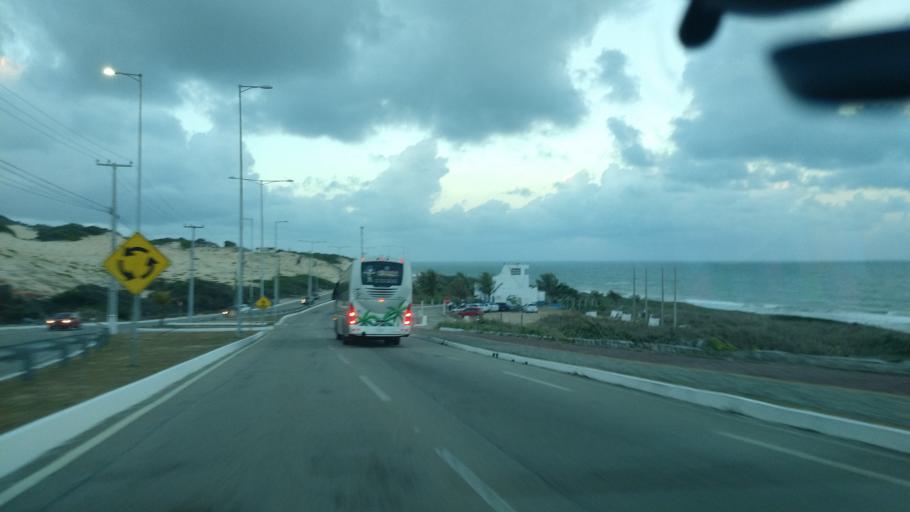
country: BR
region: Rio Grande do Norte
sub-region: Natal
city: Natal
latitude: -5.8176
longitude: -35.1831
